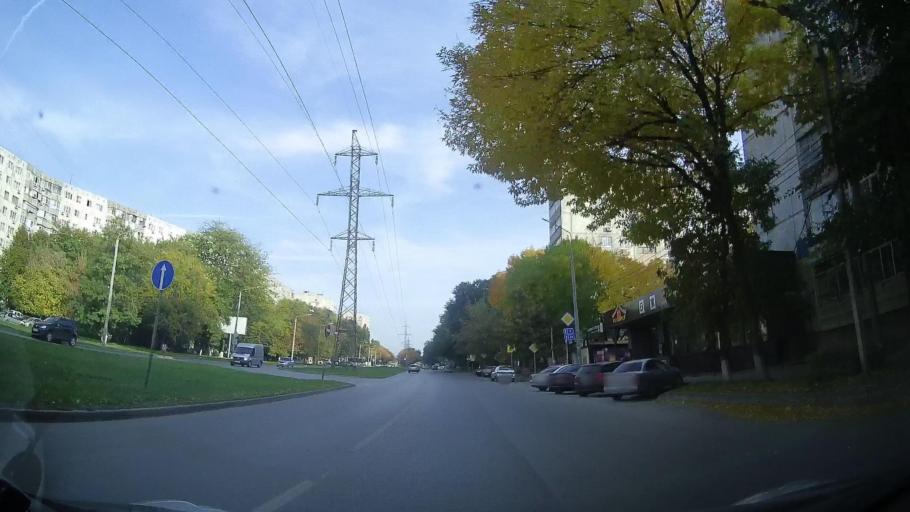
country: RU
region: Rostov
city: Imeni Chkalova
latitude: 47.2820
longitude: 39.7598
